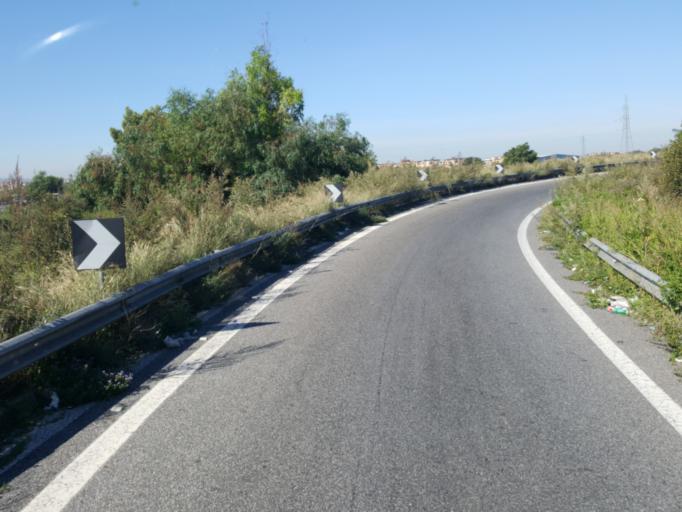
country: IT
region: Campania
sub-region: Provincia di Napoli
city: Crispano
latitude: 40.9678
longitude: 14.2908
